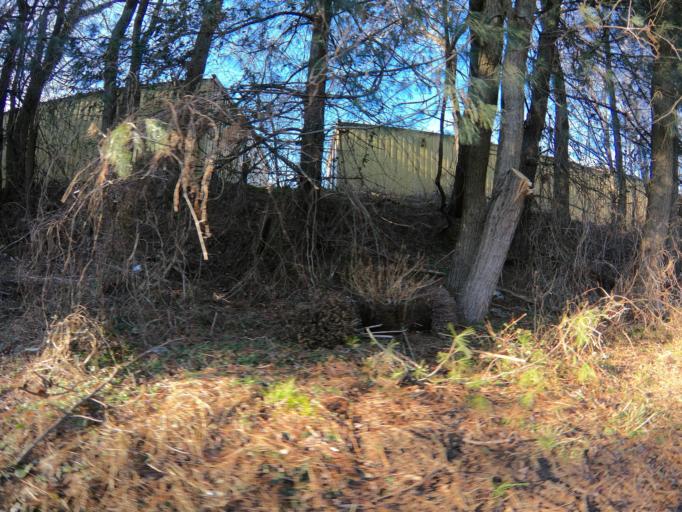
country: US
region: Maryland
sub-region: Howard County
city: Ellicott City
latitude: 39.2738
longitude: -76.8160
